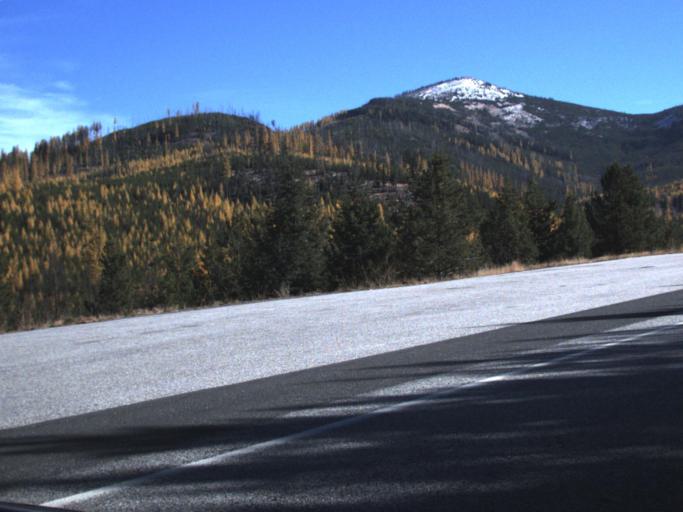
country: US
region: Washington
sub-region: Ferry County
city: Republic
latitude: 48.5989
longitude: -118.5302
